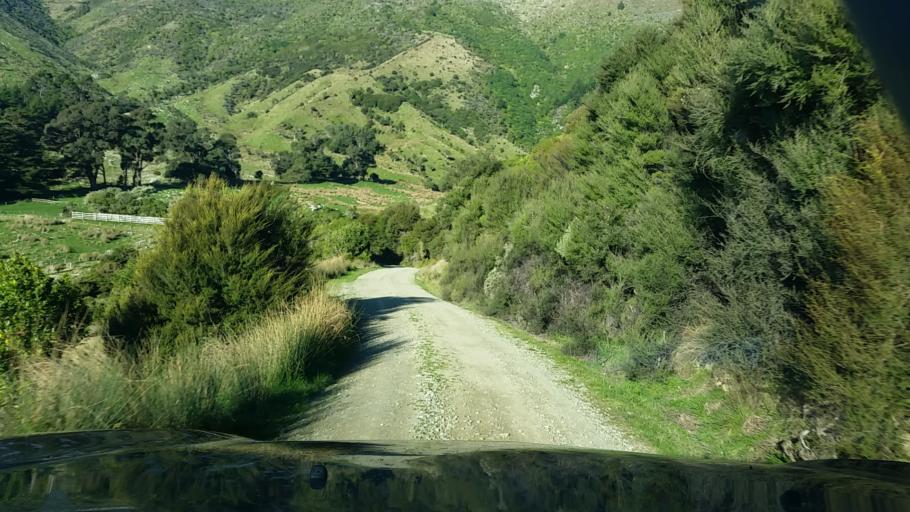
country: NZ
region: Marlborough
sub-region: Marlborough District
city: Picton
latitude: -41.0201
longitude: 174.1443
